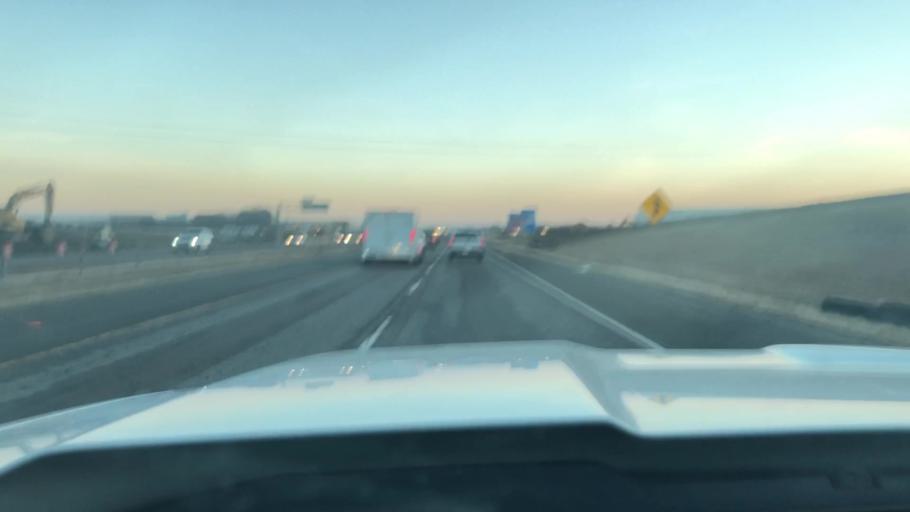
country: US
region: Texas
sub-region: Tarrant County
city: Haslet
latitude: 33.0009
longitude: -97.2926
